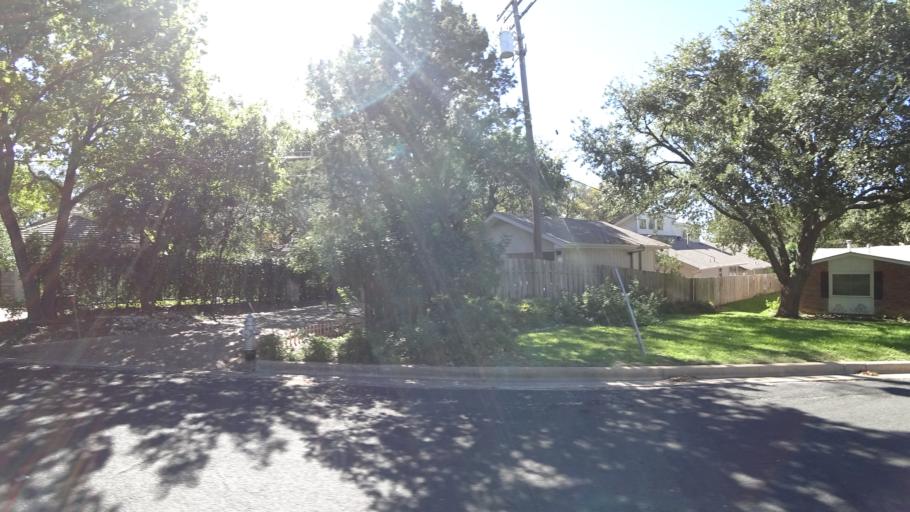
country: US
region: Texas
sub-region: Travis County
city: West Lake Hills
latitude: 30.3102
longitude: -97.7657
